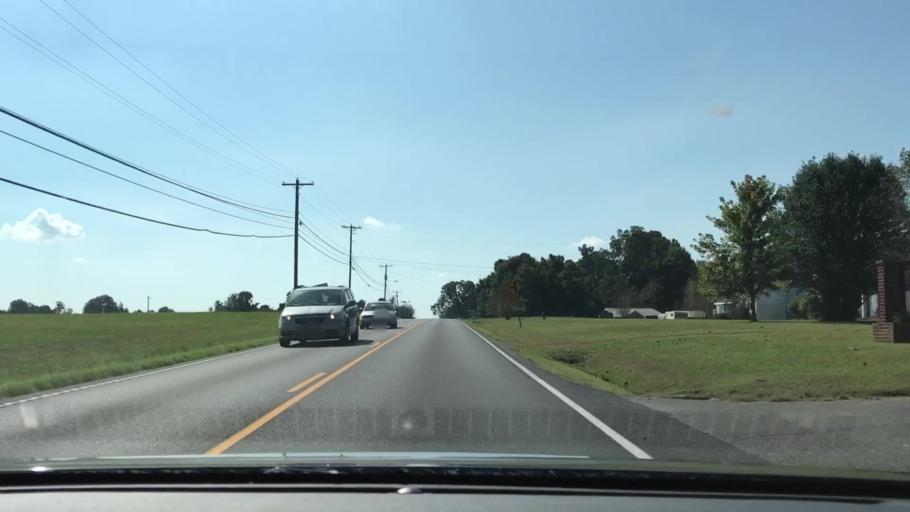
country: US
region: Kentucky
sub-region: Marshall County
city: Benton
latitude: 36.8307
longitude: -88.3506
